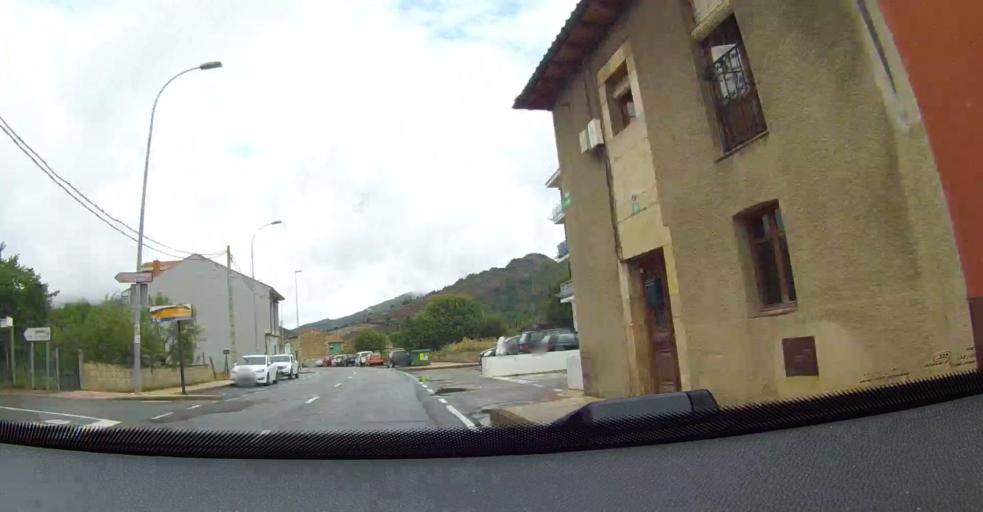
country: ES
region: Castille and Leon
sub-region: Provincia de Leon
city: Bonar
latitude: 42.8682
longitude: -5.3232
